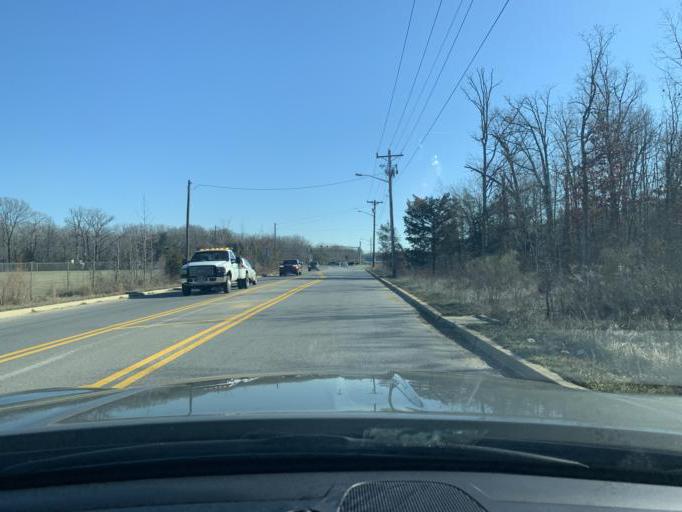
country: US
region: Maryland
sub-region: Prince George's County
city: Brandywine
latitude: 38.7002
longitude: -76.8706
